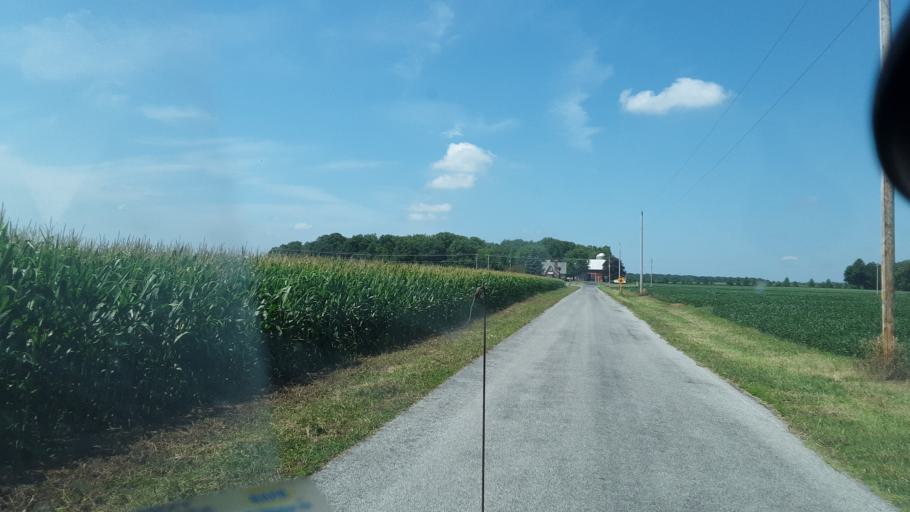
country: US
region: Ohio
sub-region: Hancock County
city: Findlay
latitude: 40.9748
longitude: -83.5521
